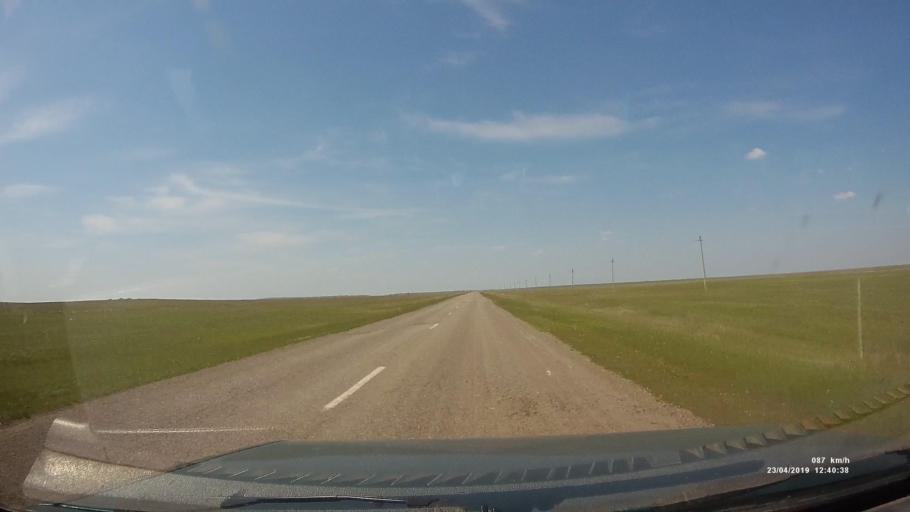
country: RU
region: Kalmykiya
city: Yashalta
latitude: 46.4418
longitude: 42.6937
